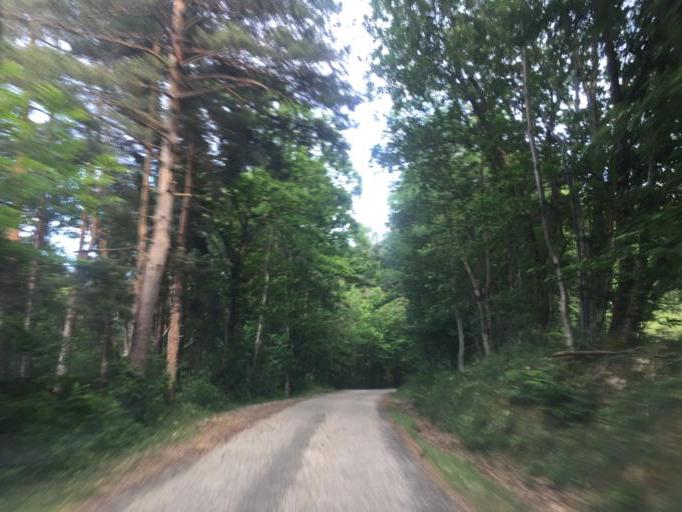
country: FR
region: Rhone-Alpes
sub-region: Departement de l'Ardeche
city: Coux
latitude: 44.7871
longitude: 4.6352
